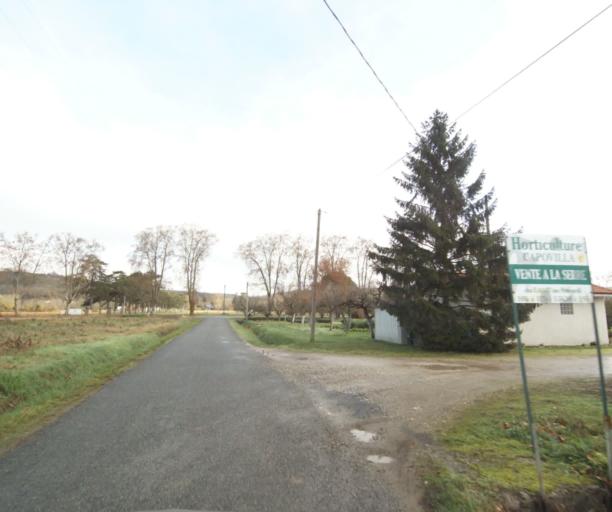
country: FR
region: Midi-Pyrenees
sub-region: Departement de la Haute-Garonne
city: Villemur-sur-Tarn
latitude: 43.8830
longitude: 1.4804
